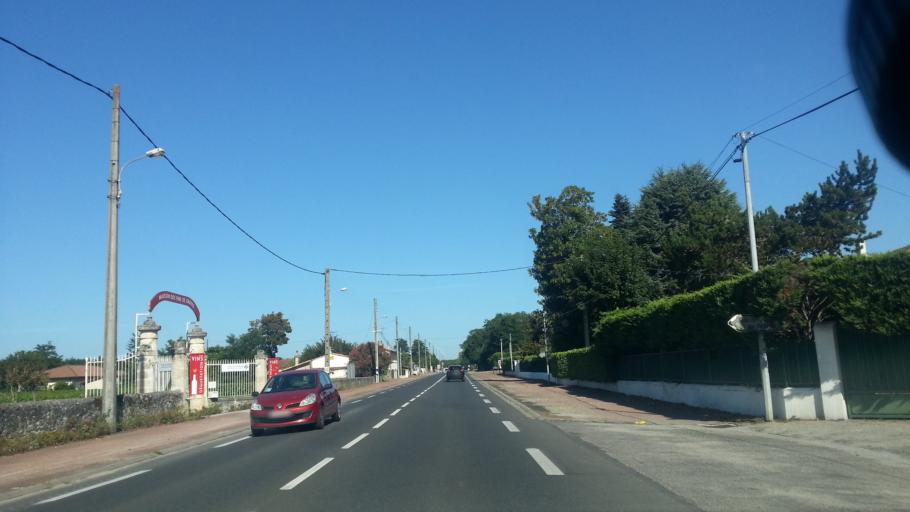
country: FR
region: Aquitaine
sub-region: Departement de la Gironde
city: Podensac
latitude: 44.6539
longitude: -0.3610
